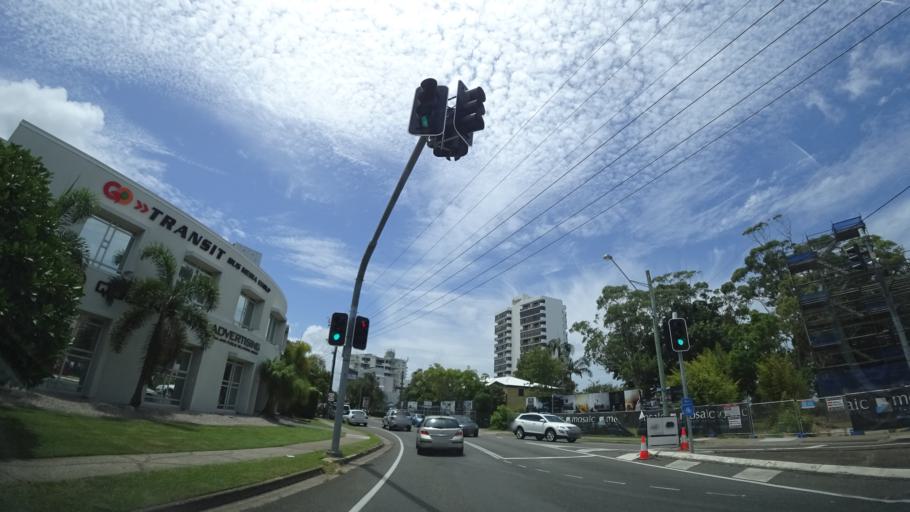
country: AU
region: Queensland
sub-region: Sunshine Coast
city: Mooloolaba
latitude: -26.6508
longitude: 153.0895
